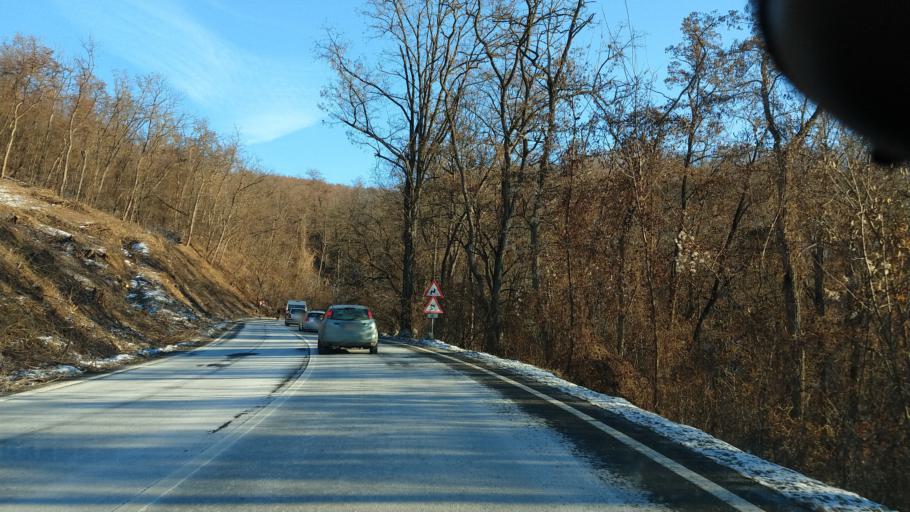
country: RO
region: Bacau
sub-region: Comuna Luizi-Calugara
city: Luizi-Calugara
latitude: 46.5429
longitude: 26.8195
